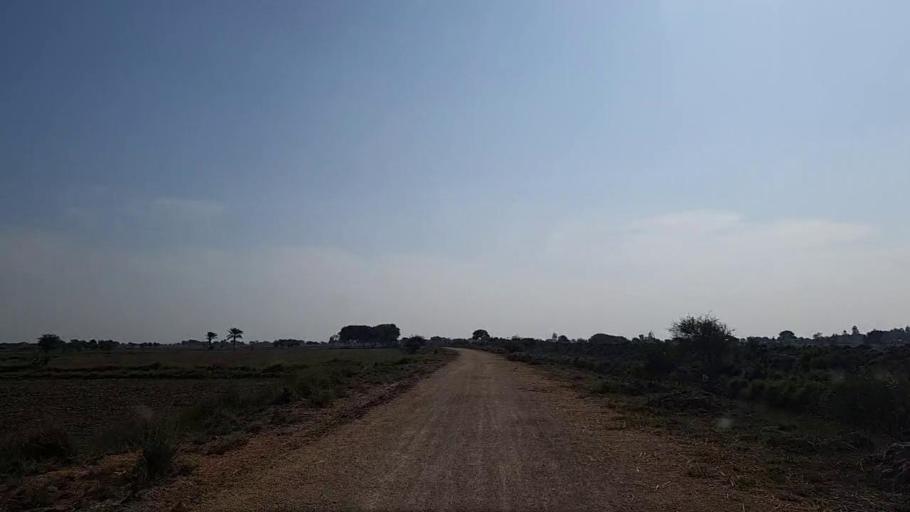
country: PK
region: Sindh
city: Daro Mehar
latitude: 24.7272
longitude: 68.1157
